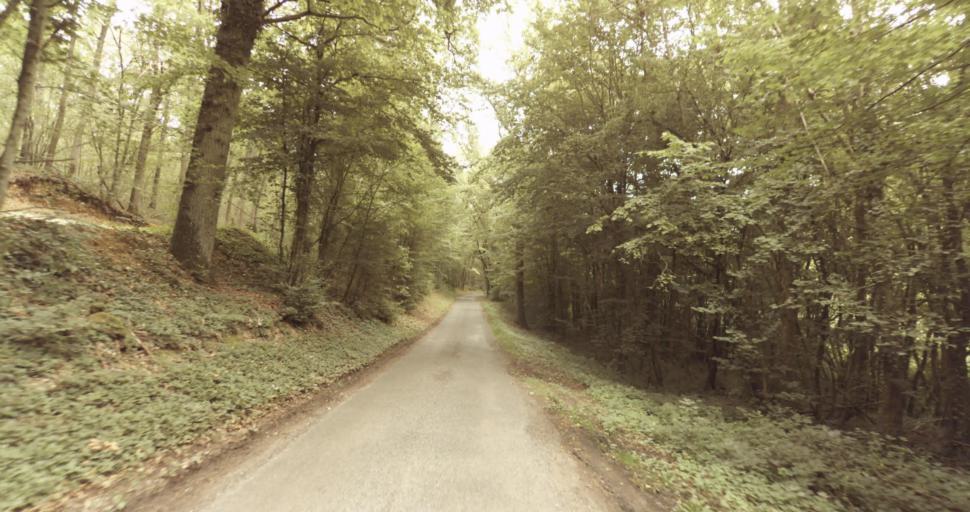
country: FR
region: Haute-Normandie
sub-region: Departement de l'Eure
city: Marcilly-sur-Eure
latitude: 48.8306
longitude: 1.3131
